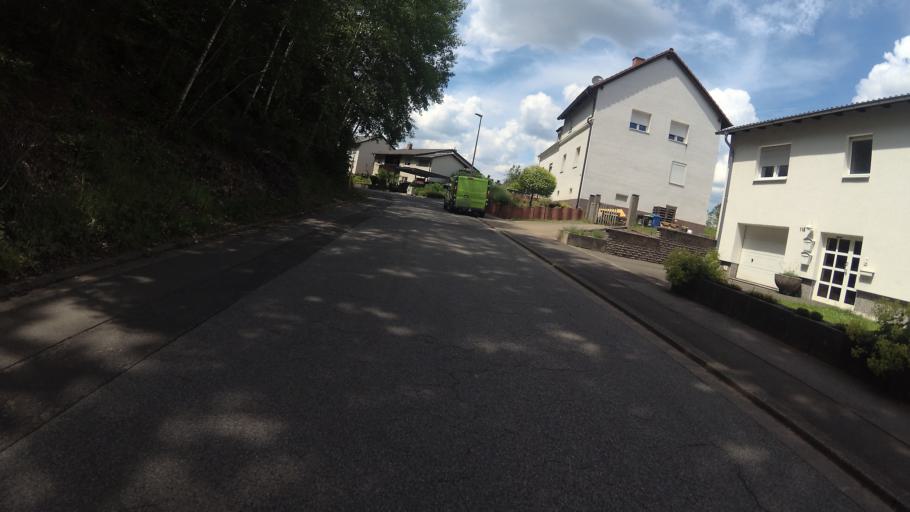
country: DE
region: Saarland
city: Homburg
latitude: 49.3092
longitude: 7.3723
